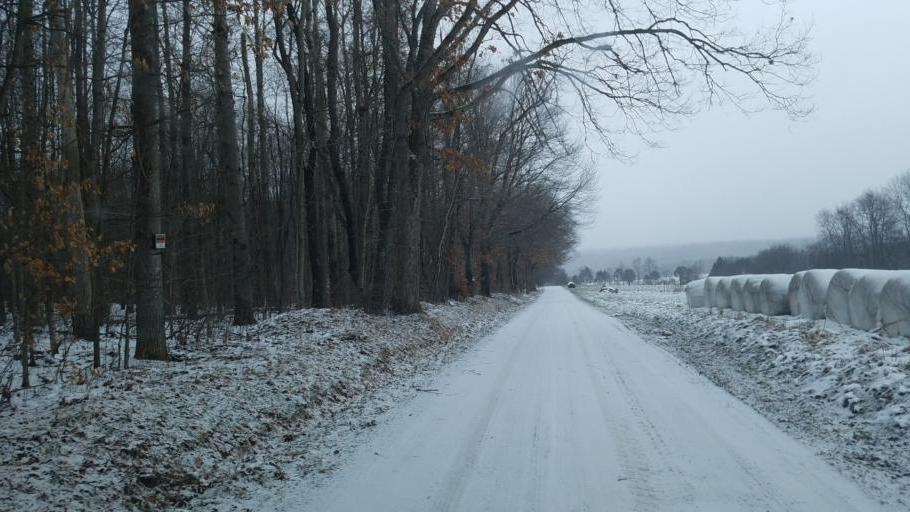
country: US
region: Pennsylvania
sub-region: Crawford County
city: Cochranton
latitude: 41.4629
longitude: -79.9718
